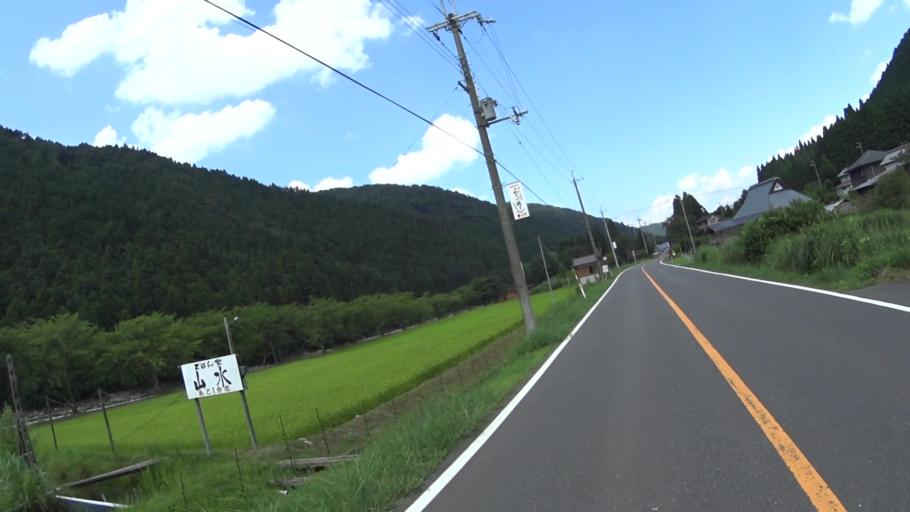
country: JP
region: Shiga Prefecture
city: Kitahama
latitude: 35.3204
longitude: 135.8966
